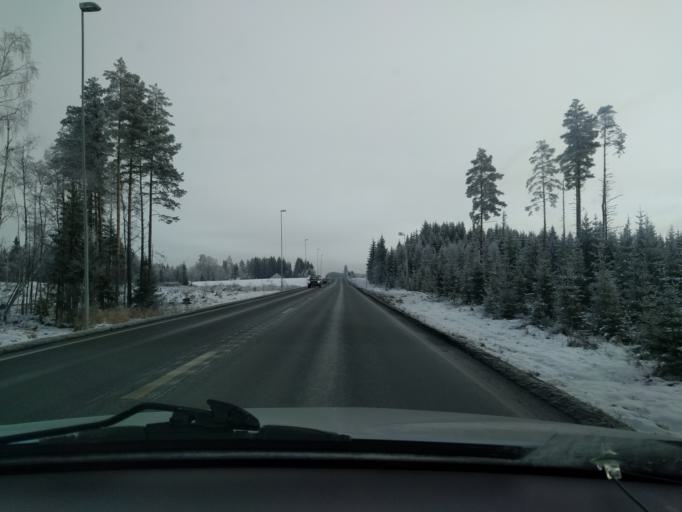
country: NO
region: Hedmark
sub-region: Loten
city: Loten
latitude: 60.8526
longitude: 11.3800
